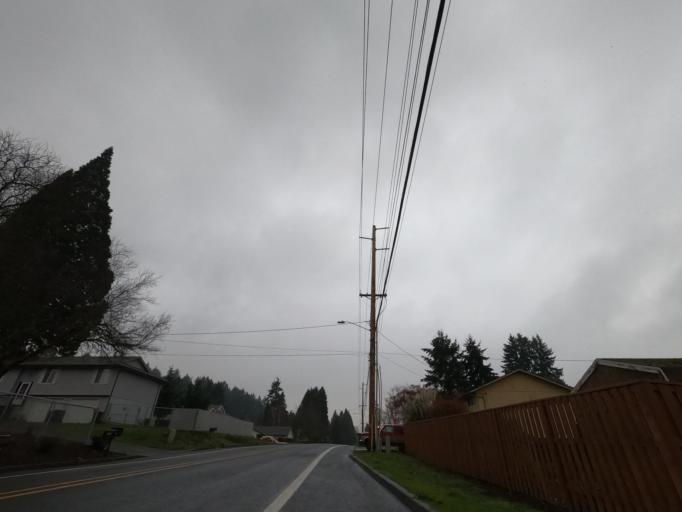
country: US
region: Oregon
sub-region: Clackamas County
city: Clackamas
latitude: 45.3986
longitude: -122.5757
